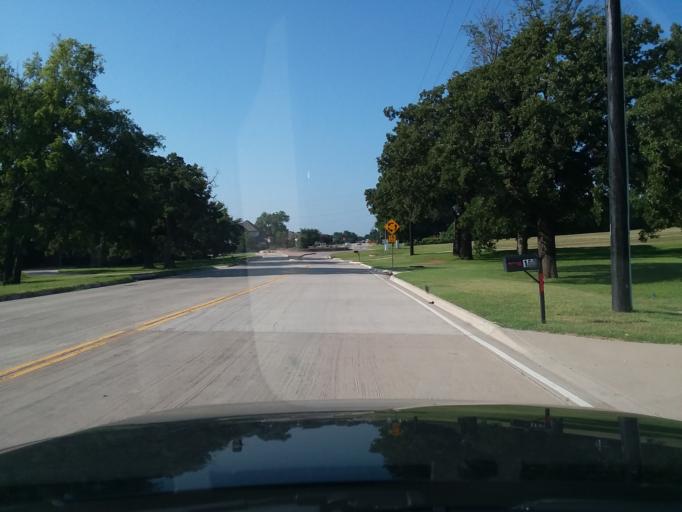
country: US
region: Texas
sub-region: Denton County
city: Double Oak
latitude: 33.0676
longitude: -97.0881
